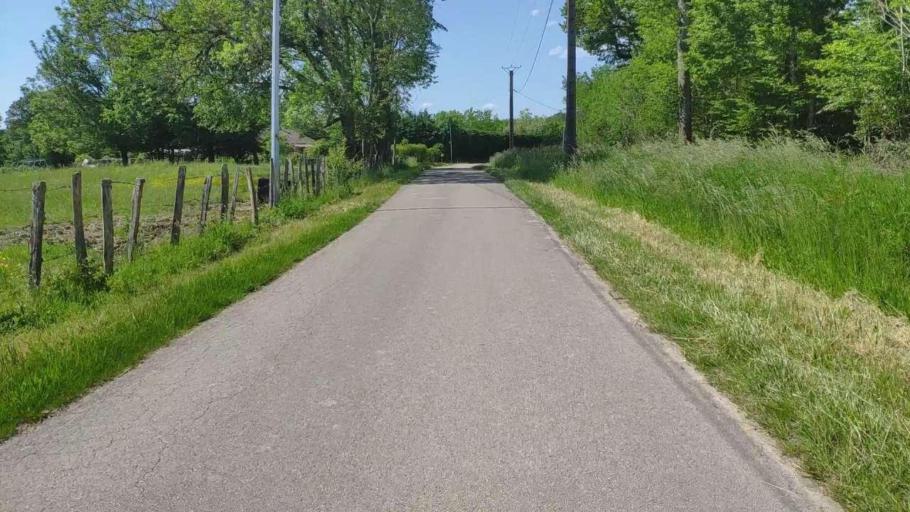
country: FR
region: Franche-Comte
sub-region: Departement du Jura
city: Bletterans
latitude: 46.8122
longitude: 5.4095
